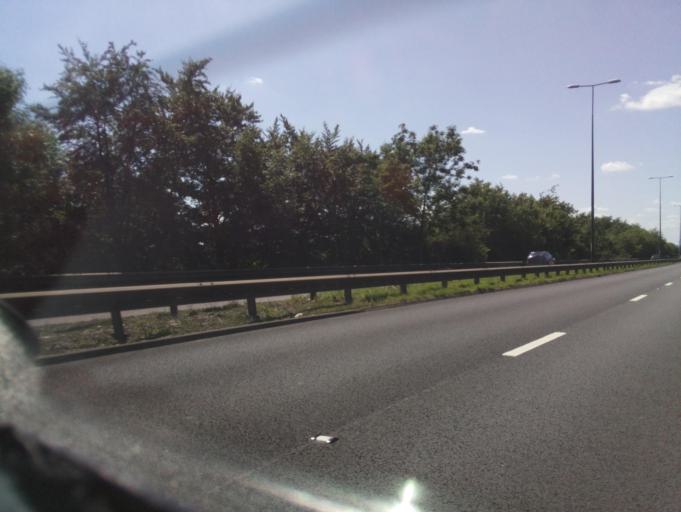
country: GB
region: England
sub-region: Derbyshire
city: Borrowash
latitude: 52.9120
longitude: -1.3486
